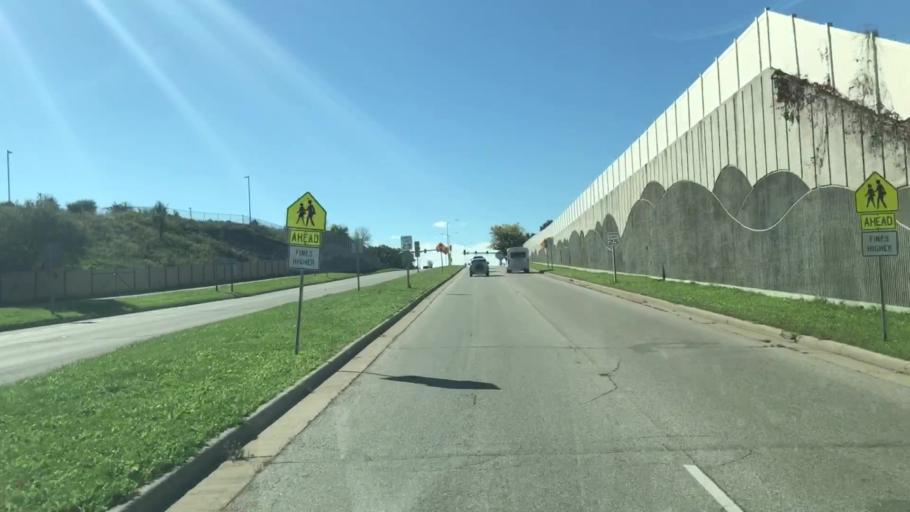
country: US
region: Wisconsin
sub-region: Waukesha County
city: Pewaukee
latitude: 43.0469
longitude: -88.2858
